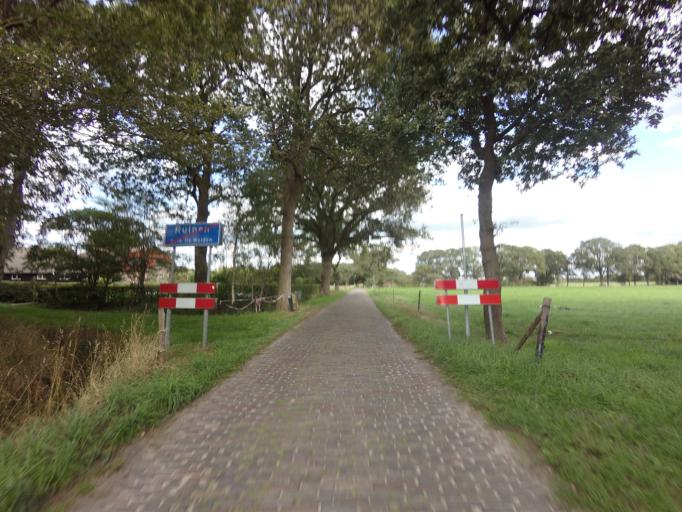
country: NL
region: Drenthe
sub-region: Gemeente De Wolden
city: Ruinen
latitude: 52.7682
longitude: 6.3652
